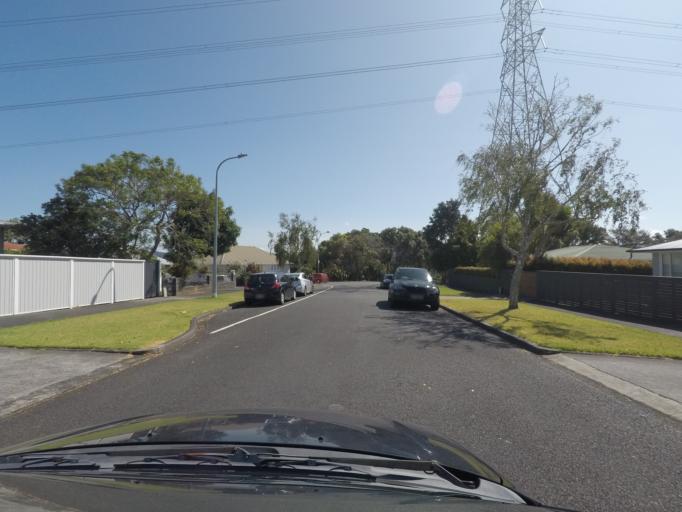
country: NZ
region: Auckland
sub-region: Auckland
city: Rosebank
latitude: -36.8891
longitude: 174.6735
